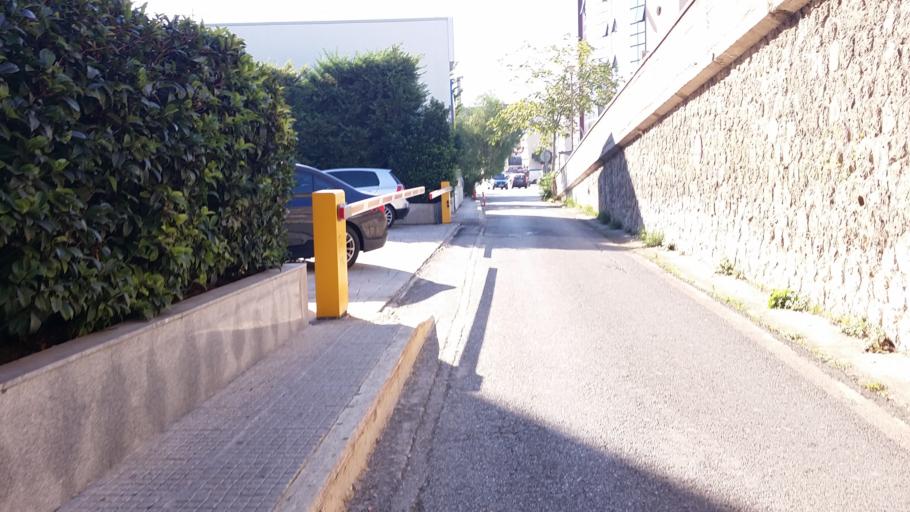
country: GR
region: Attica
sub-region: Nomarchia Athinas
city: Nea Ionia
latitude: 38.0439
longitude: 23.7598
